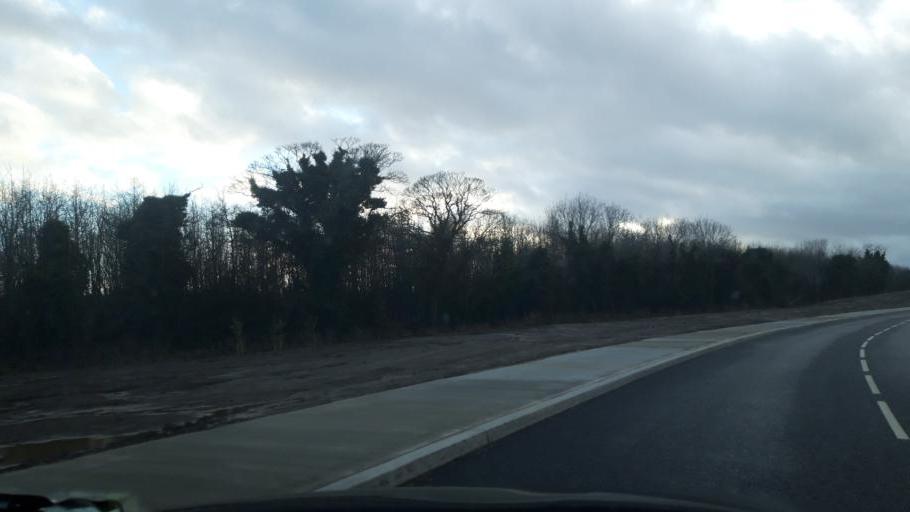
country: IE
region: Leinster
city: Donabate
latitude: 53.4791
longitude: -6.1416
